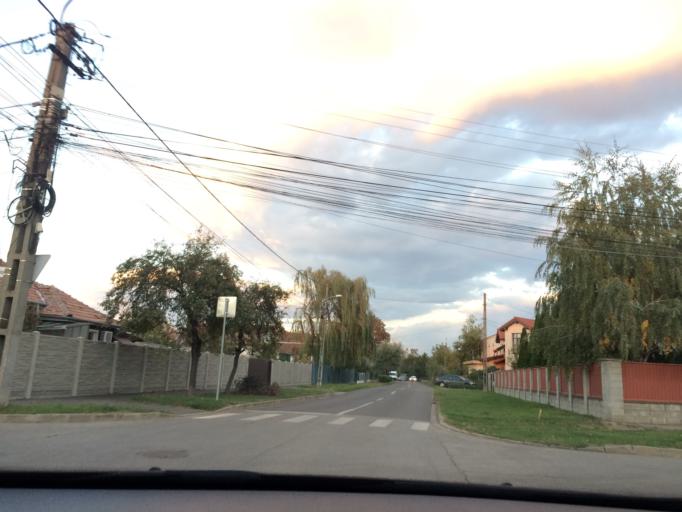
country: RO
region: Timis
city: Timisoara
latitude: 45.7564
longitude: 21.1907
